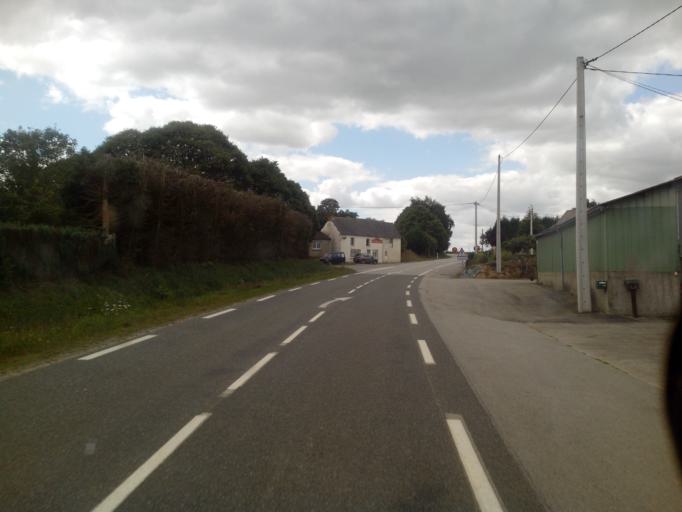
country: FR
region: Brittany
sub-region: Departement du Morbihan
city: Meneac
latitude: 48.1299
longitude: -2.4790
